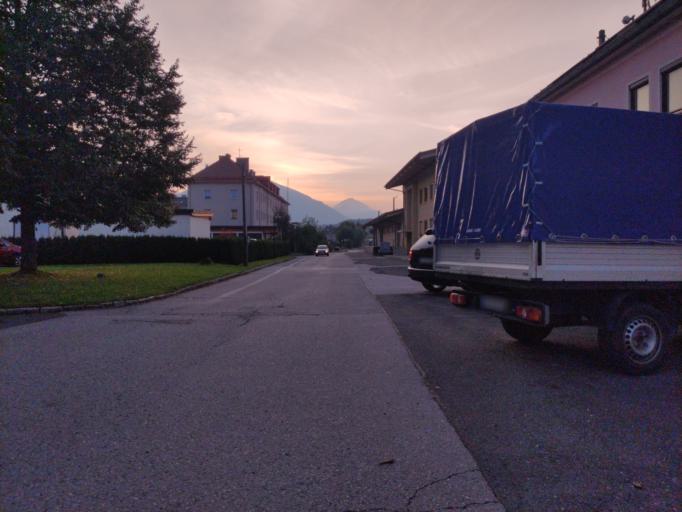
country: AT
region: Carinthia
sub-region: Politischer Bezirk Villach Land
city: Arnoldstein
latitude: 46.5512
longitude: 13.7069
